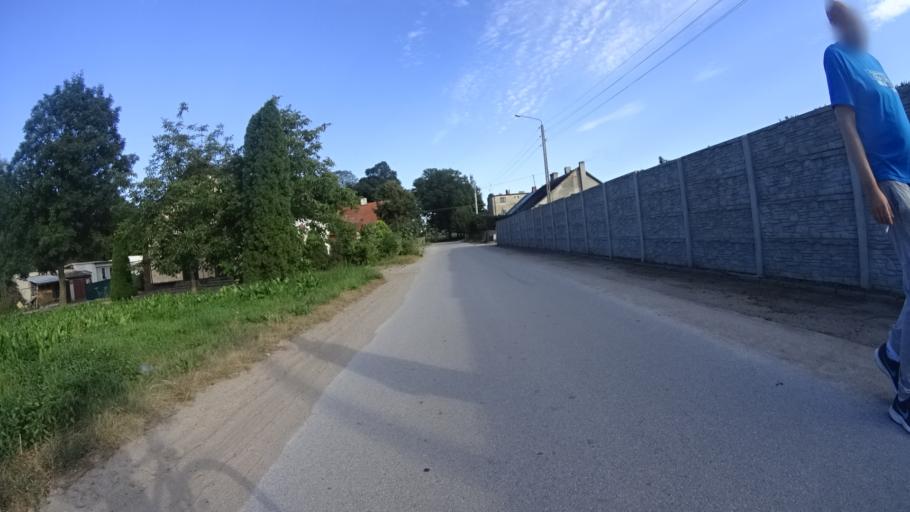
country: PL
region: Masovian Voivodeship
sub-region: Powiat grojecki
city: Goszczyn
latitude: 51.6920
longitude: 20.8190
